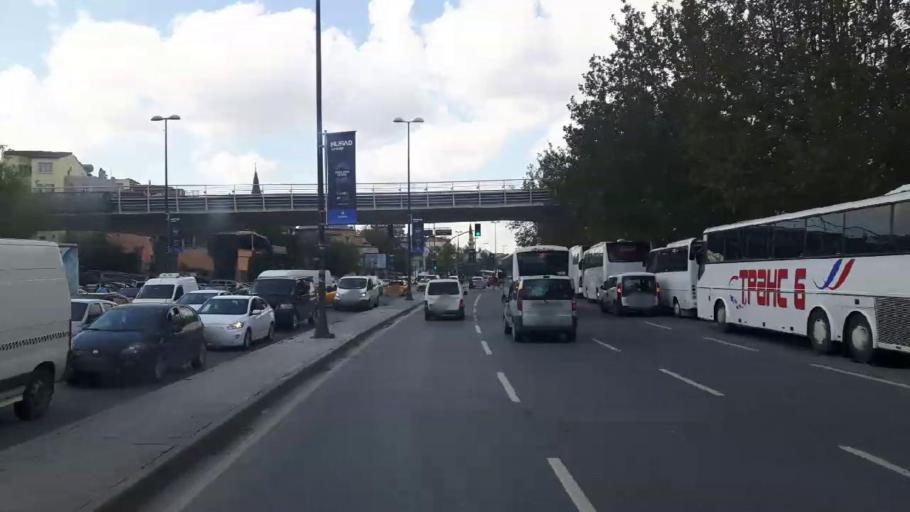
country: TR
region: Istanbul
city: Eminoenue
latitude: 41.0196
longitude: 28.9649
